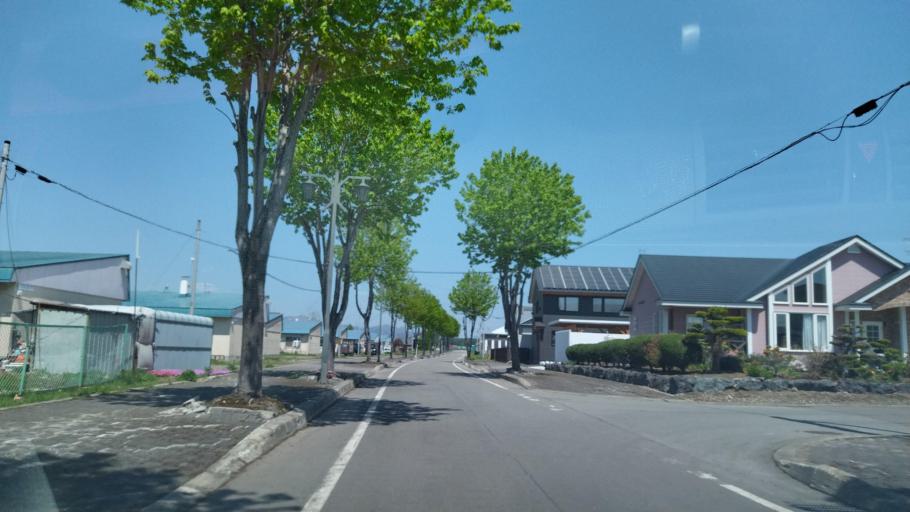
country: JP
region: Hokkaido
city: Otofuke
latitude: 43.1716
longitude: 143.2511
